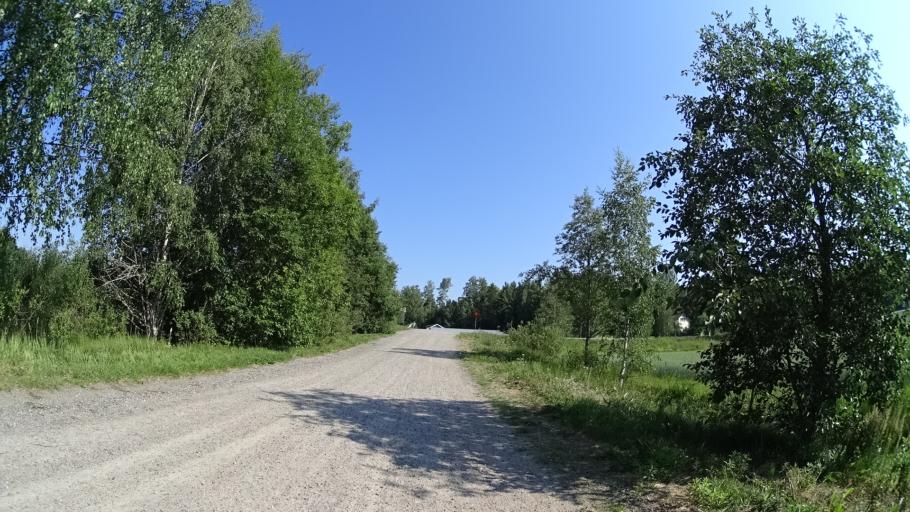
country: FI
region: Uusimaa
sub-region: Helsinki
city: Kerava
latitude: 60.3593
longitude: 25.1245
